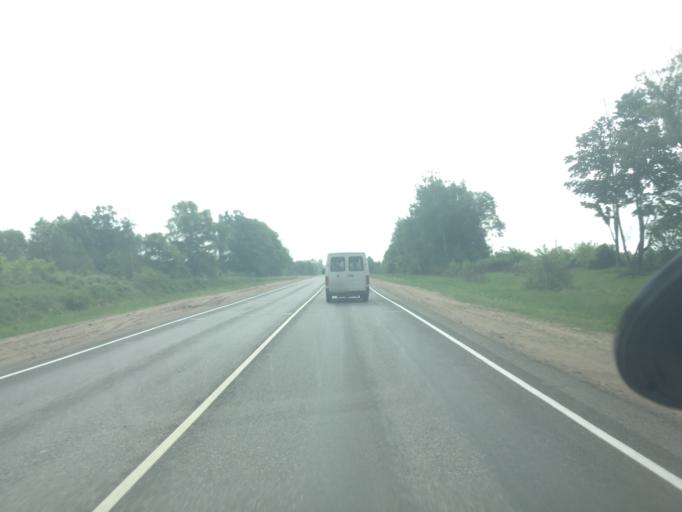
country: RU
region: Smolensk
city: Golynki
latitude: 54.8686
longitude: 31.3494
